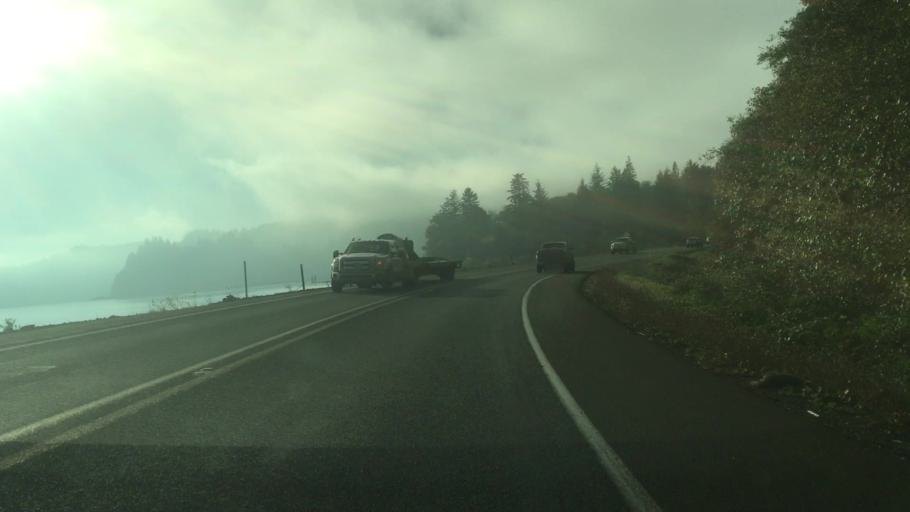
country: US
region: Oregon
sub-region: Clatsop County
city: Astoria
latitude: 46.2698
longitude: -123.8197
